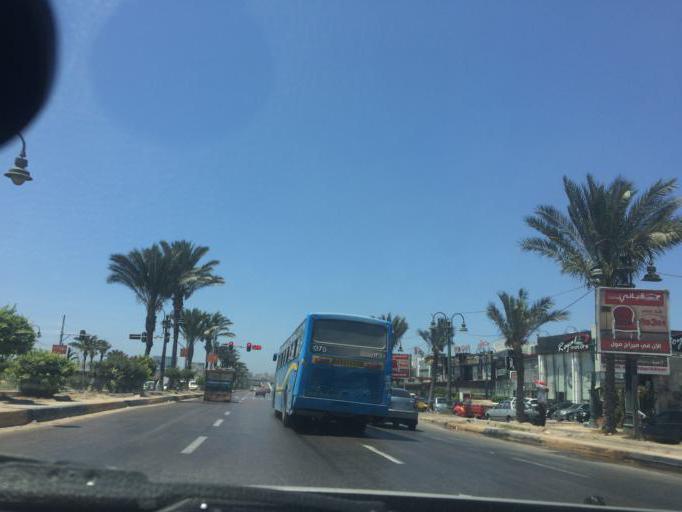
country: EG
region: Alexandria
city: Alexandria
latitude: 31.1732
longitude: 29.9326
